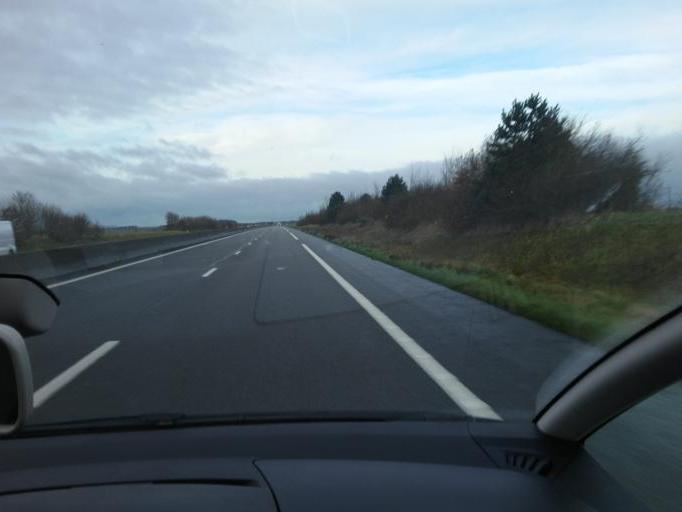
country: FR
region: Picardie
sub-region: Departement de la Somme
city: Harbonnieres
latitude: 49.8570
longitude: 2.6985
